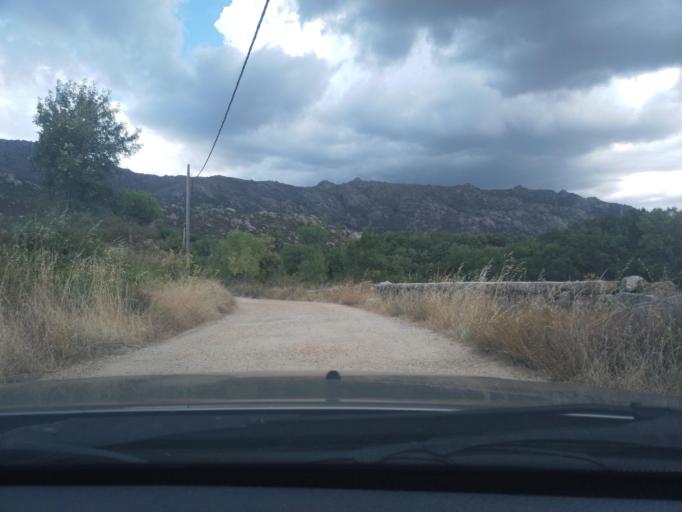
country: ES
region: Madrid
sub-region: Provincia de Madrid
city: Becerril de la Sierra
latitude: 40.7335
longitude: -3.9590
